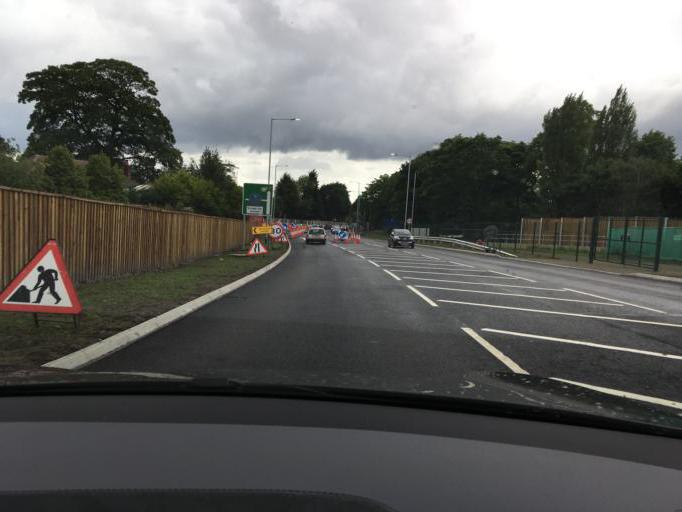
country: GB
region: England
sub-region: Borough of Stockport
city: Hazel Grove
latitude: 53.3721
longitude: -2.1043
